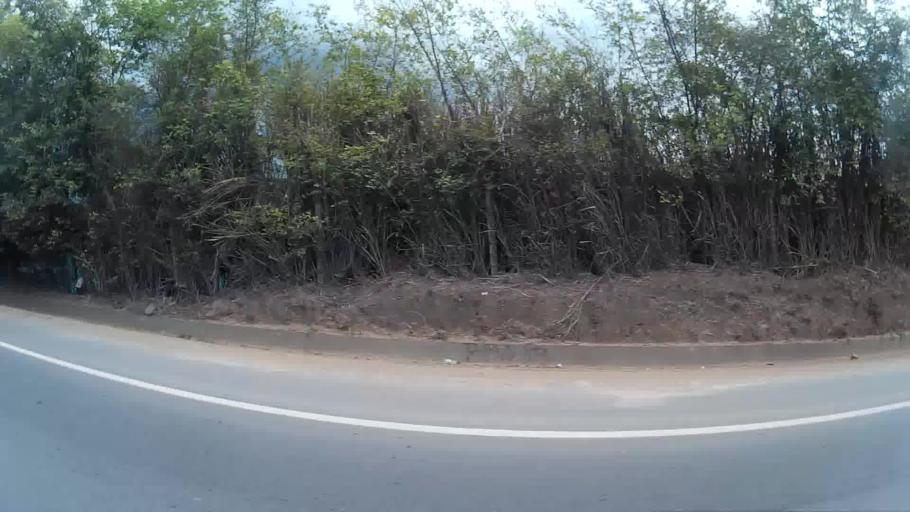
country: CO
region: Risaralda
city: Pereira
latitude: 4.8106
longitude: -75.7732
